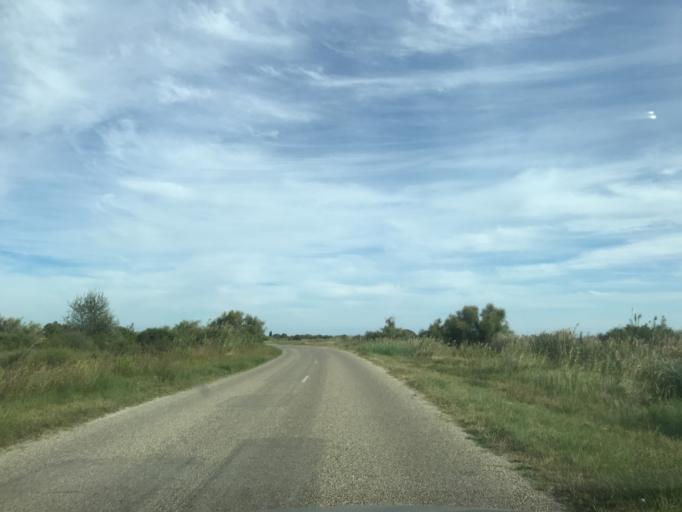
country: FR
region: Provence-Alpes-Cote d'Azur
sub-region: Departement des Bouches-du-Rhone
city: Saintes-Maries-de-la-Mer
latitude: 43.5222
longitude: 4.3862
